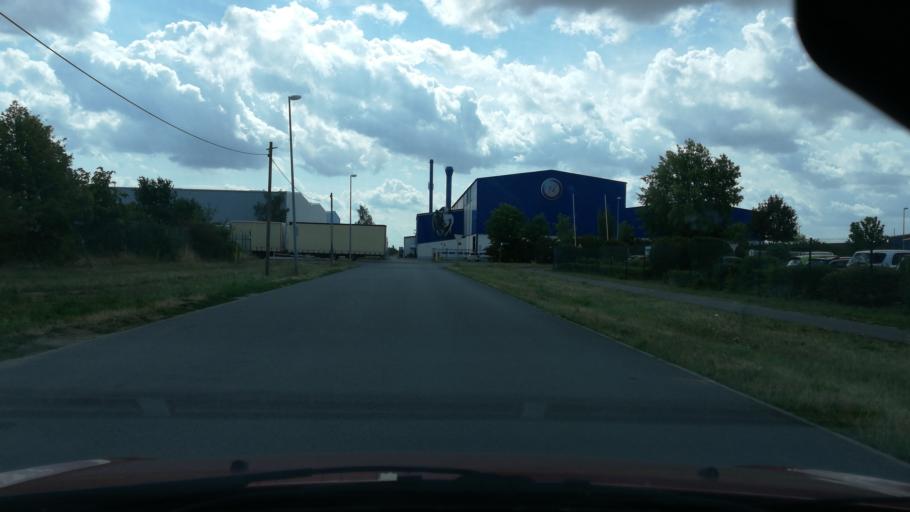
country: DE
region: Saxony-Anhalt
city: Landsberg
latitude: 51.5385
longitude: 12.1688
